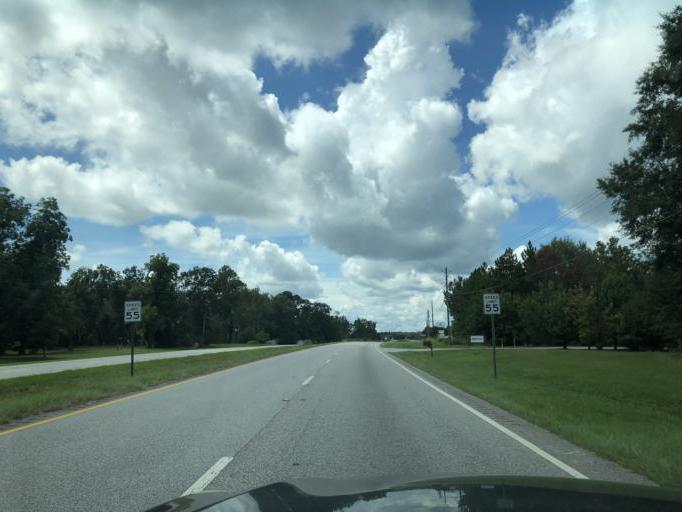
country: US
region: Alabama
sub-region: Barbour County
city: Eufaula
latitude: 31.9302
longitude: -85.1401
